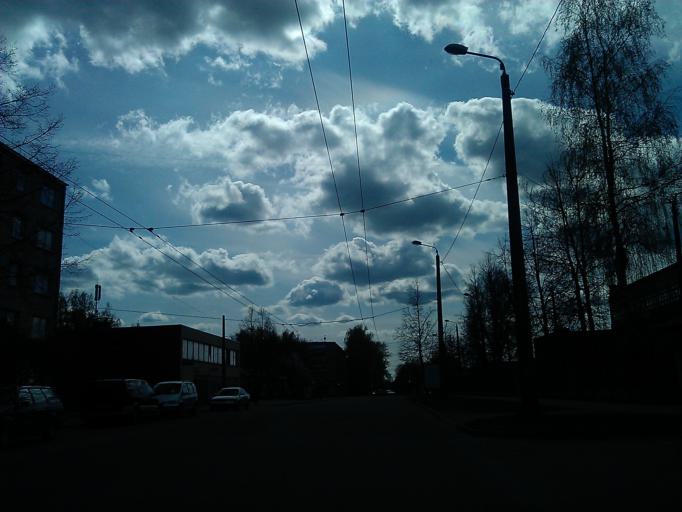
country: LV
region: Kekava
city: Balozi
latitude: 56.9161
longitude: 24.1863
